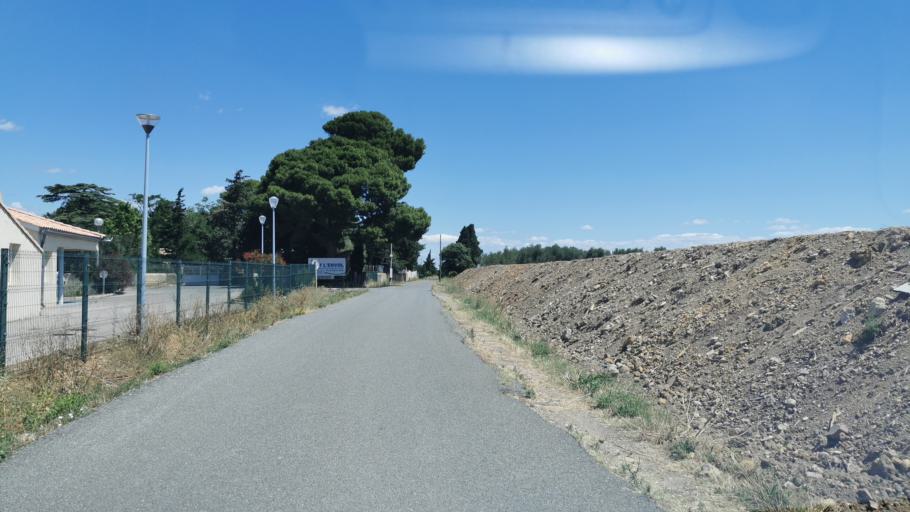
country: FR
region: Languedoc-Roussillon
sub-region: Departement de l'Aude
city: Narbonne
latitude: 43.1597
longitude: 2.9953
